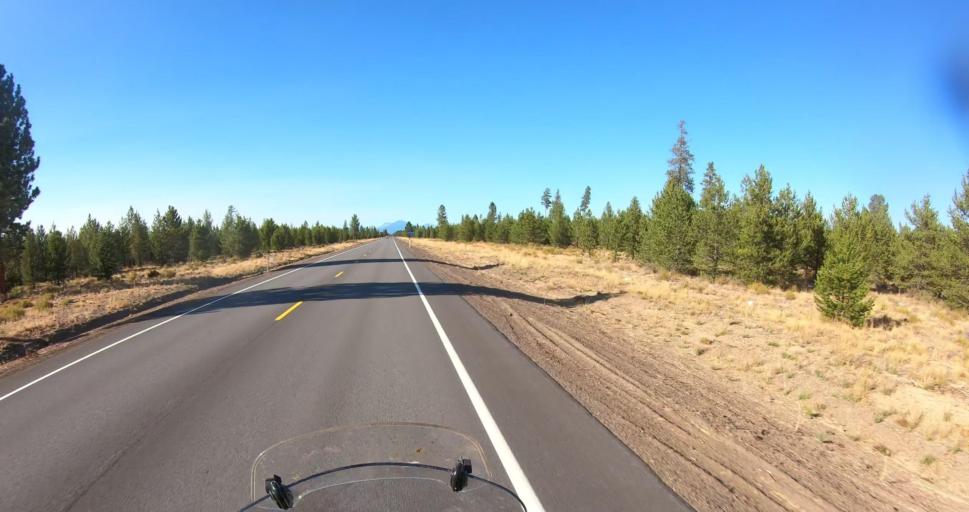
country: US
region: Oregon
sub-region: Deschutes County
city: La Pine
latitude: 43.6194
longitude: -121.5077
